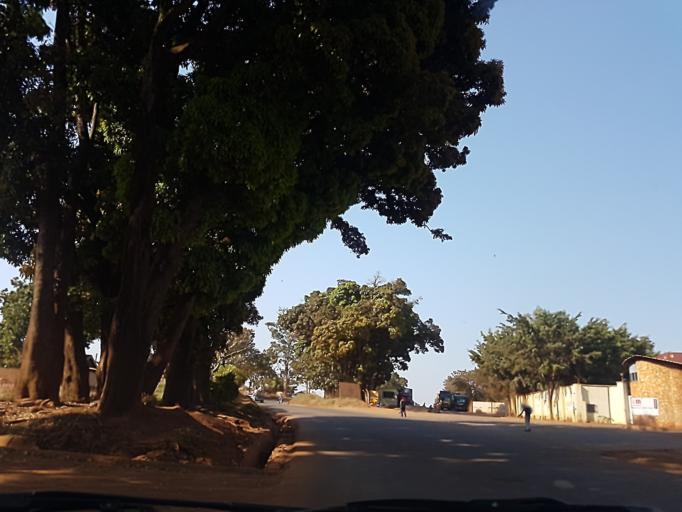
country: UG
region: Central Region
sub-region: Wakiso District
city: Kireka
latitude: 0.3367
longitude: 32.6151
